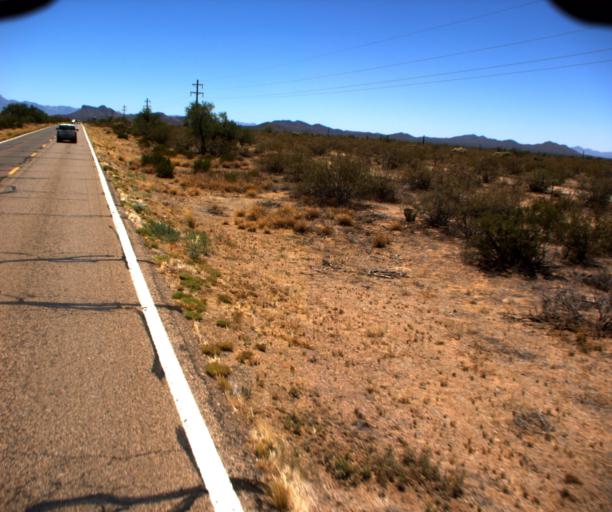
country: US
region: Arizona
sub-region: Pima County
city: Sells
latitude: 31.9457
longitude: -111.9297
